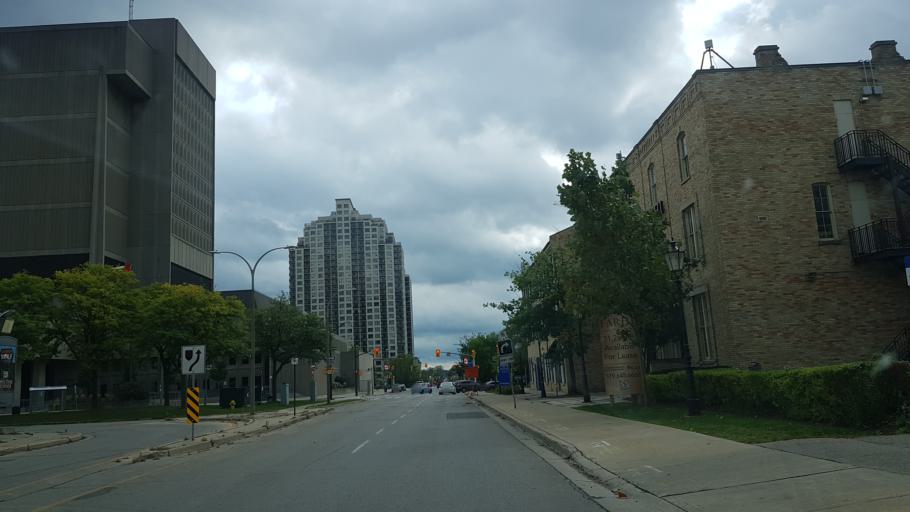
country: CA
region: Ontario
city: London
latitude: 42.9842
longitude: -81.2549
